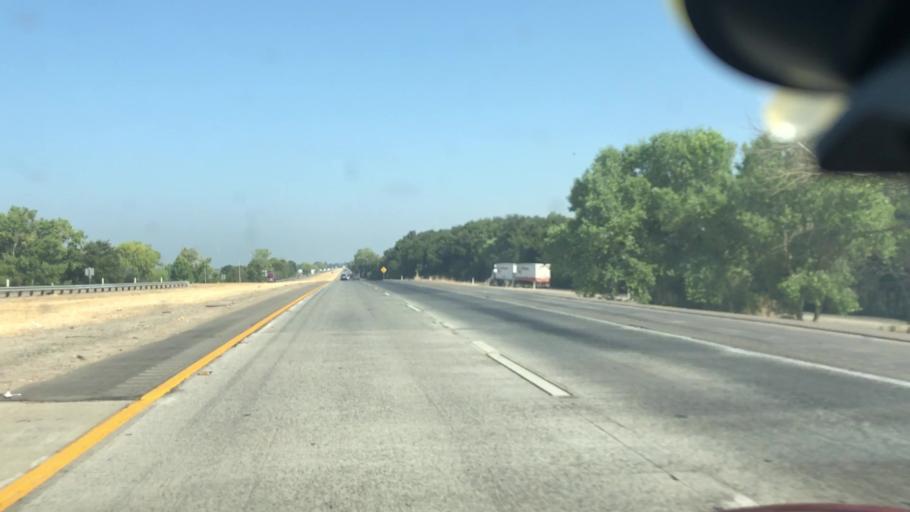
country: US
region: California
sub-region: San Joaquin County
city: Thornton
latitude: 38.2268
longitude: -121.4309
